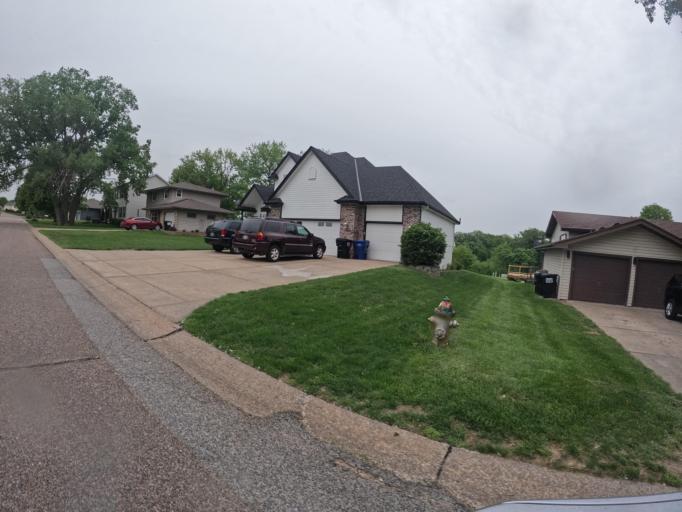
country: US
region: Nebraska
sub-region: Sarpy County
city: Offutt Air Force Base
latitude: 41.0465
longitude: -95.9719
